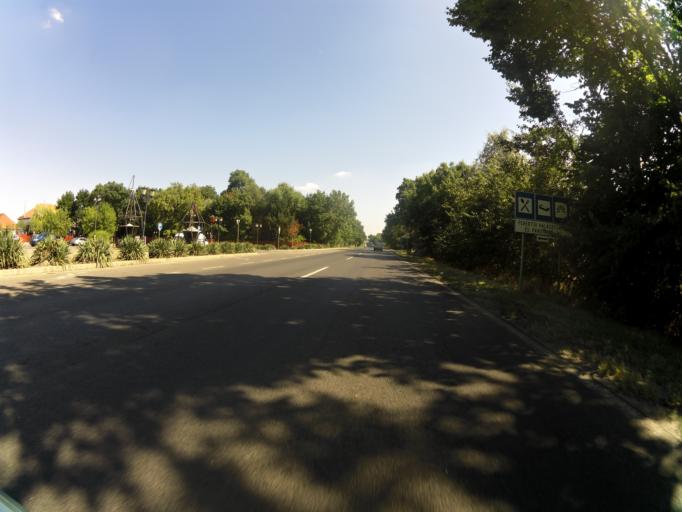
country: HU
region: Csongrad
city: Szatymaz
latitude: 46.3035
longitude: 20.0710
